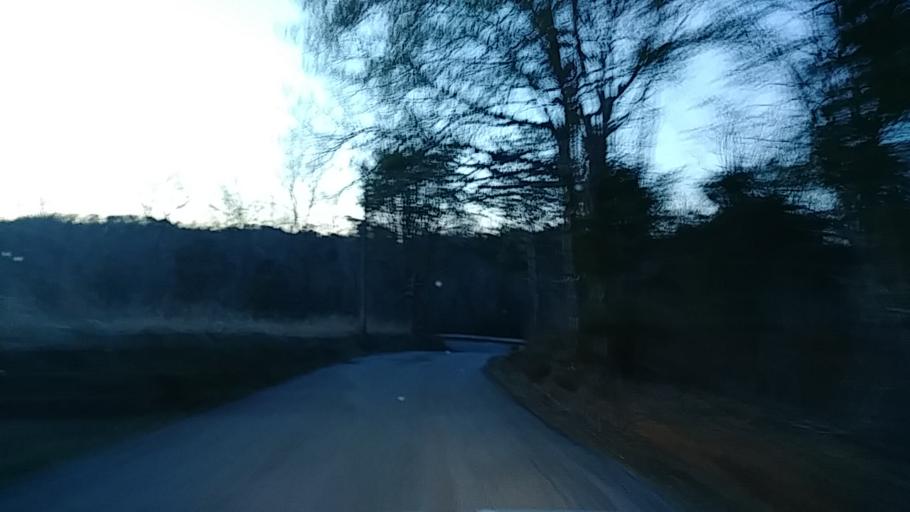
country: US
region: Tennessee
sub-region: Greene County
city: Mosheim
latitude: 36.0637
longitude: -82.9832
